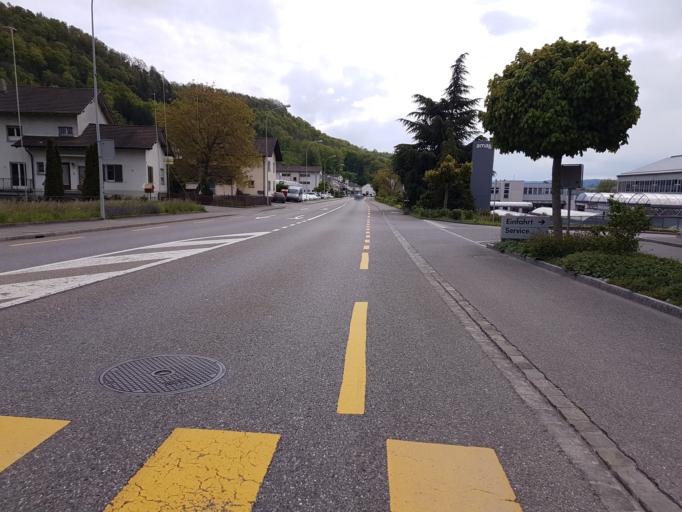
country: CH
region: Aargau
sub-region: Bezirk Brugg
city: Schinznach Bad
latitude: 47.4477
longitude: 8.1686
